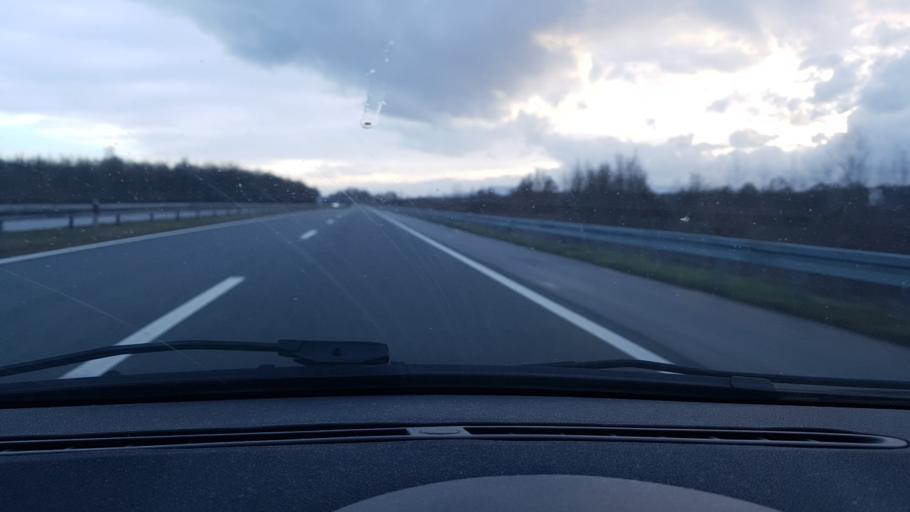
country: HR
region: Zagrebacka
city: Pojatno
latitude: 45.9197
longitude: 15.8244
